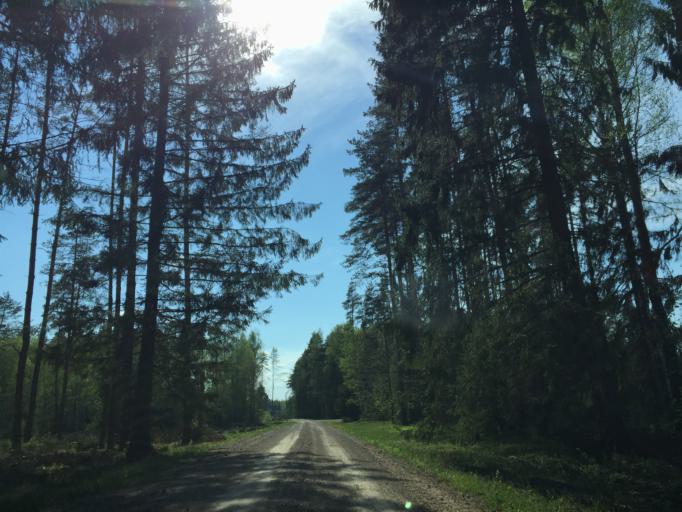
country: LV
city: Tireli
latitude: 56.8180
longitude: 23.6940
